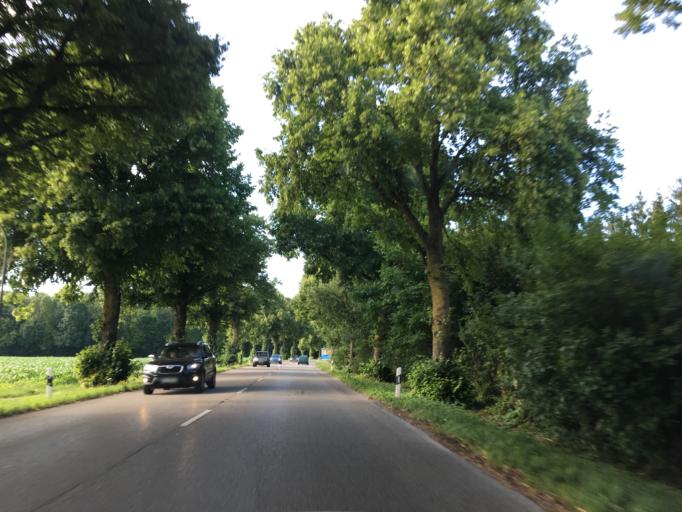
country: DE
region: Bavaria
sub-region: Upper Bavaria
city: Erding
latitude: 48.2893
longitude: 11.8990
